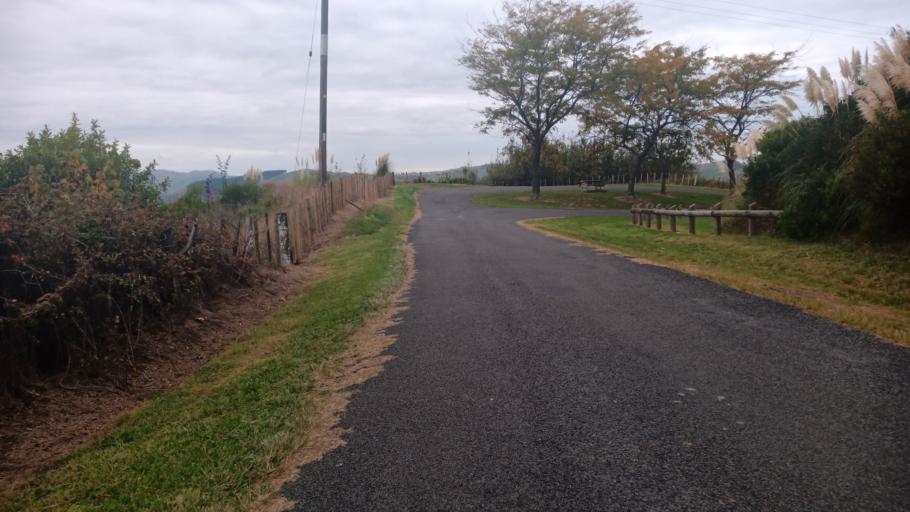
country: NZ
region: Gisborne
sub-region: Gisborne District
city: Gisborne
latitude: -38.6803
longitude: 178.0346
